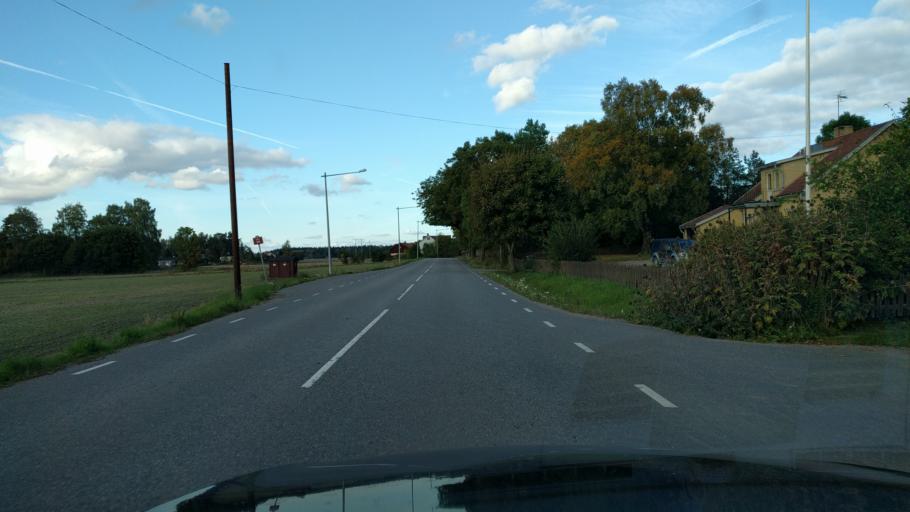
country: SE
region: Uppsala
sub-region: Osthammars Kommun
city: Bjorklinge
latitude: 60.1533
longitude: 17.5890
